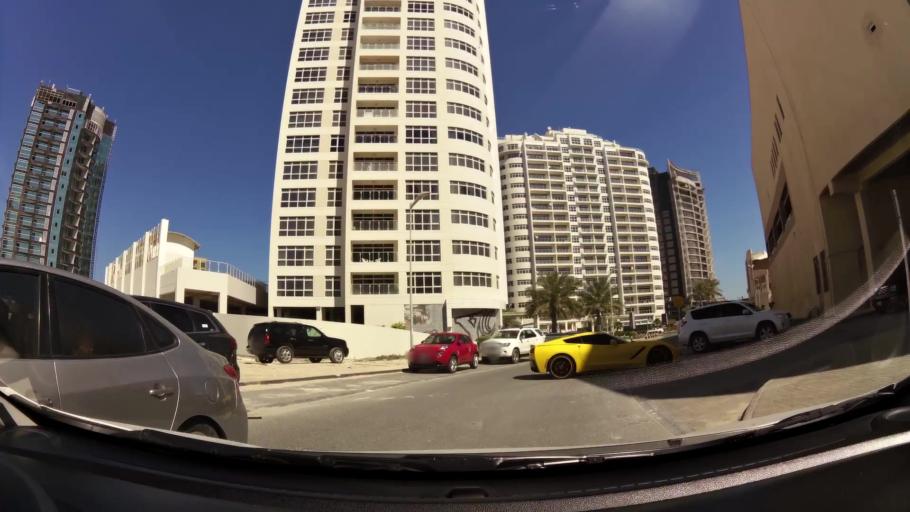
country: BH
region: Muharraq
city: Al Hadd
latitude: 26.2906
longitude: 50.6635
